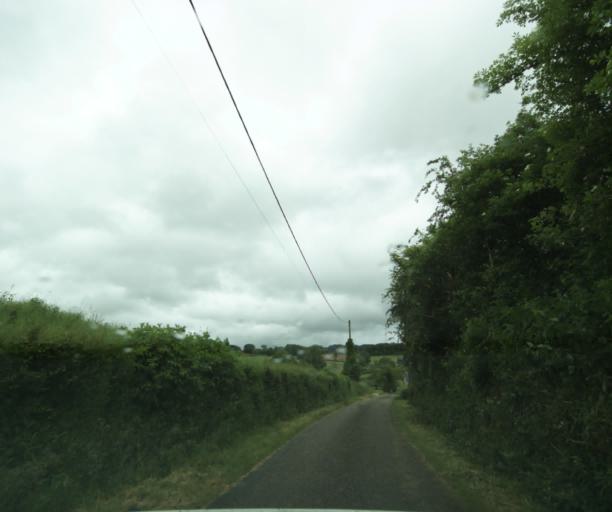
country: FR
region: Bourgogne
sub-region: Departement de Saone-et-Loire
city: Charolles
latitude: 46.4391
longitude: 4.4265
